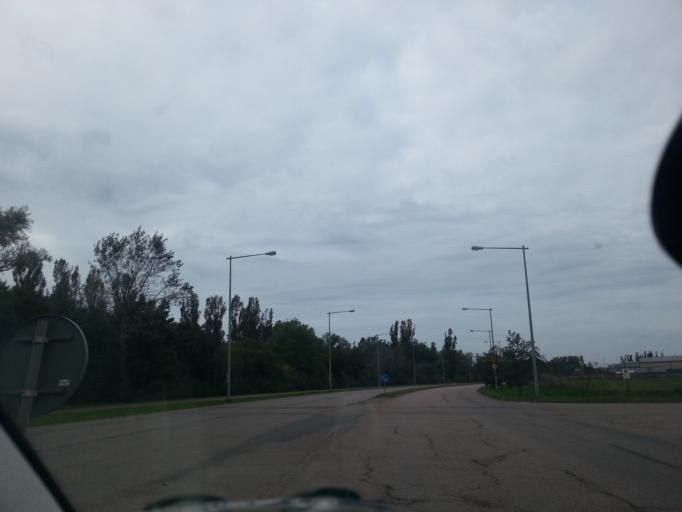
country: SE
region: Skane
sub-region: Landskrona
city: Landskrona
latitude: 55.8646
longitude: 12.8670
